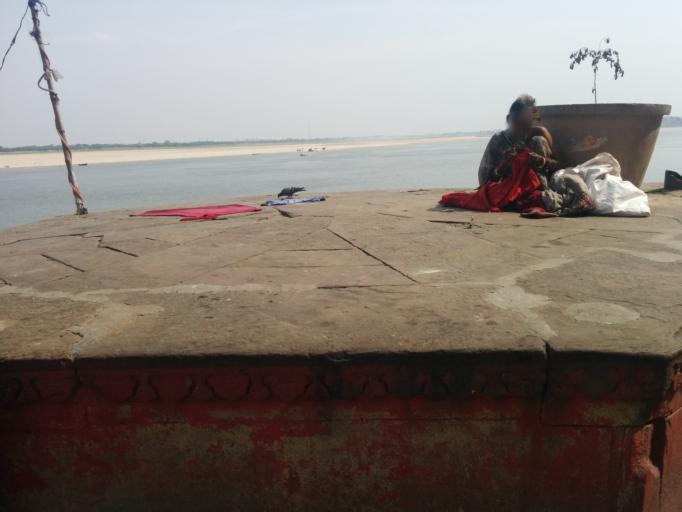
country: IN
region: Uttar Pradesh
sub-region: Varanasi
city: Varanasi
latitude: 25.3057
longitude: 83.0099
